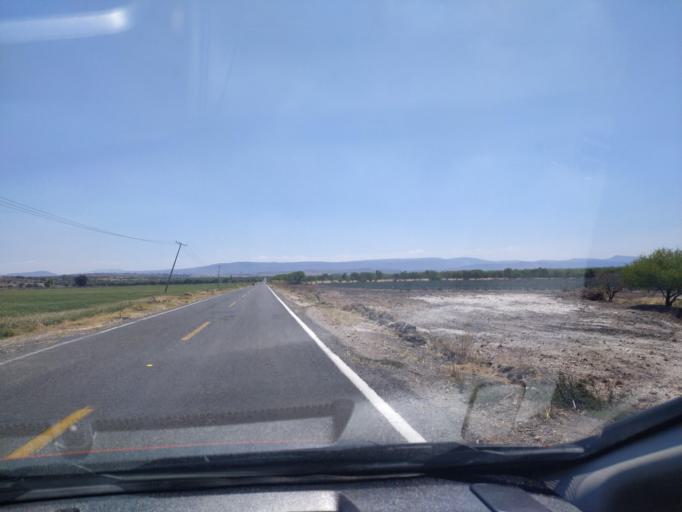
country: MX
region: Guanajuato
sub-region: San Francisco del Rincon
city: San Ignacio de Hidalgo
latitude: 20.7858
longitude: -101.8347
